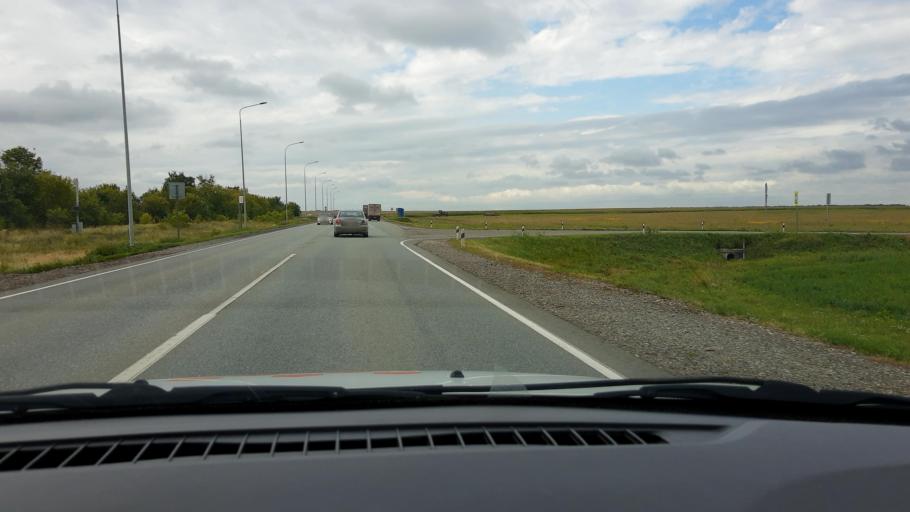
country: RU
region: Tatarstan
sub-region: Alekseyevskiy Rayon
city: Alekseyevskoye
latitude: 55.3139
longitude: 50.2846
